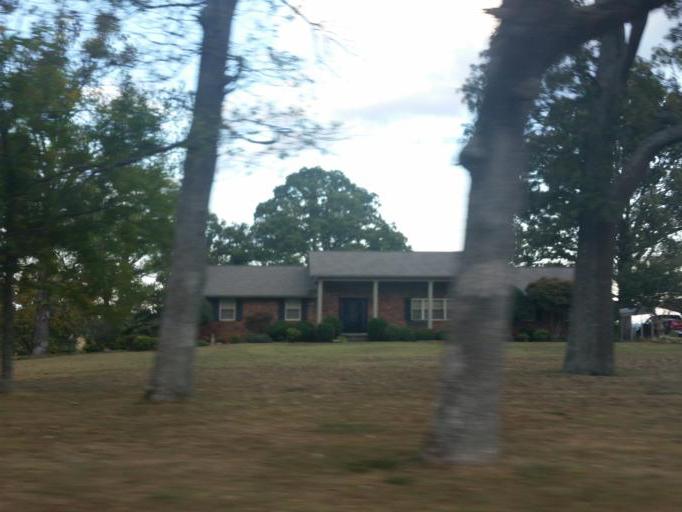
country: US
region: Tennessee
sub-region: Blount County
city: Louisville
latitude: 35.7685
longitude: -84.0274
